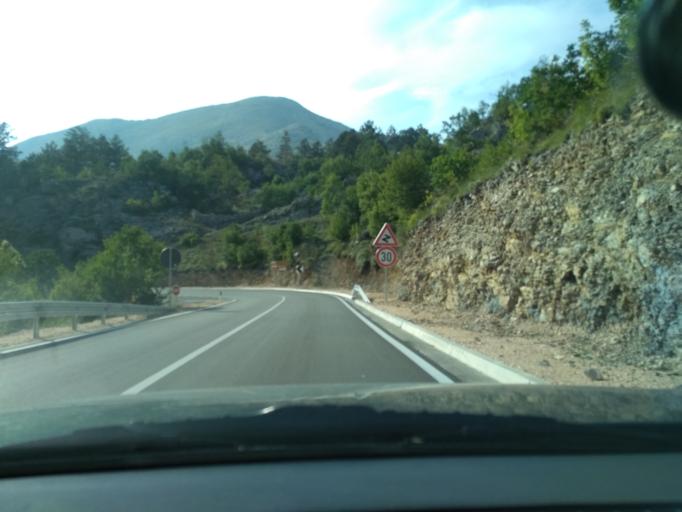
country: ME
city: Dobrota
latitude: 42.4387
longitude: 18.8324
